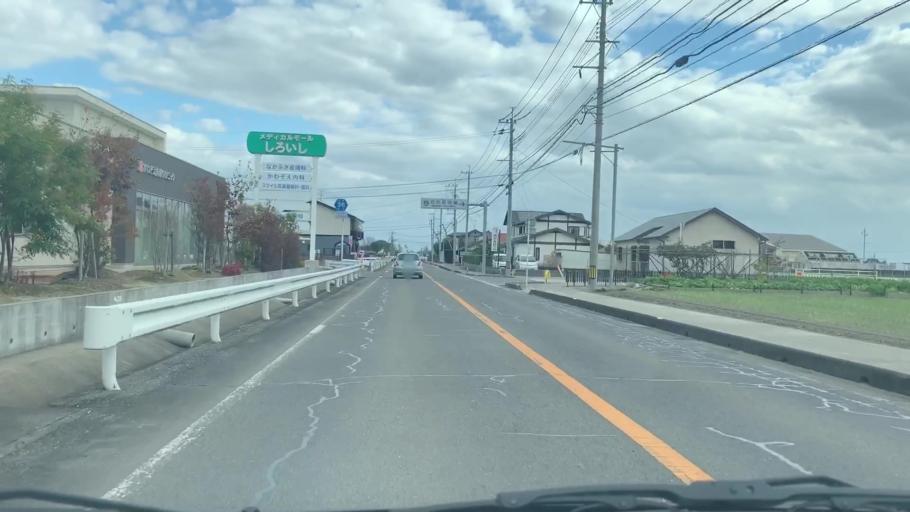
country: JP
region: Saga Prefecture
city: Kashima
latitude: 33.1860
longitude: 130.1473
